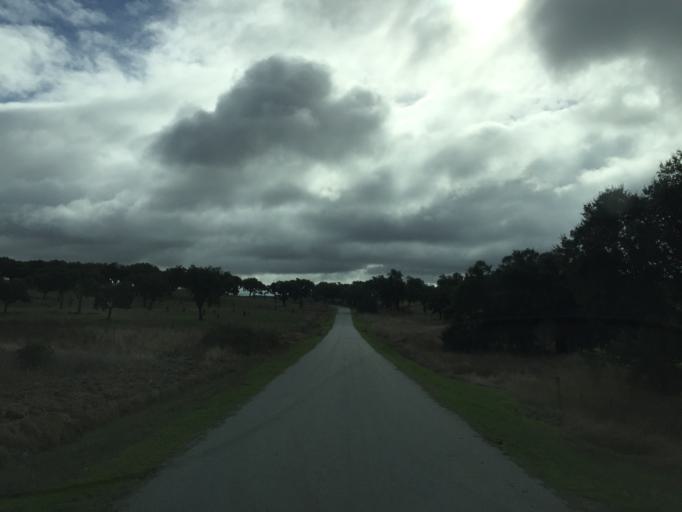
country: PT
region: Portalegre
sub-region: Alter do Chao
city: Alter do Chao
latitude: 39.2347
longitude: -7.6884
